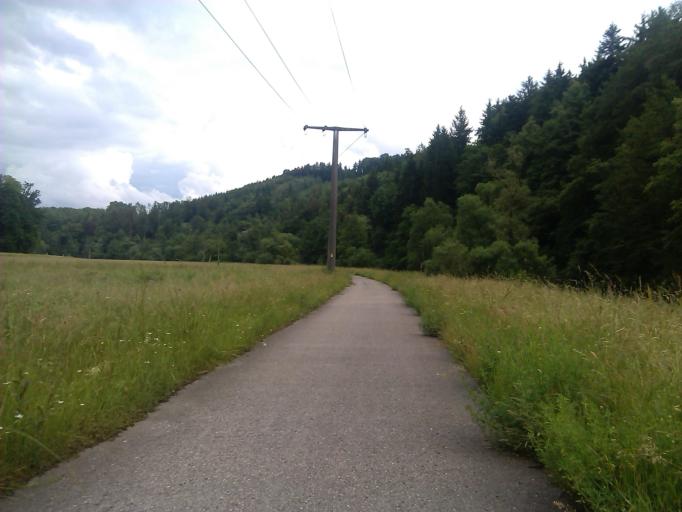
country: DE
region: Baden-Wuerttemberg
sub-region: Regierungsbezirk Stuttgart
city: Obergroningen
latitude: 48.9090
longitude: 9.9296
